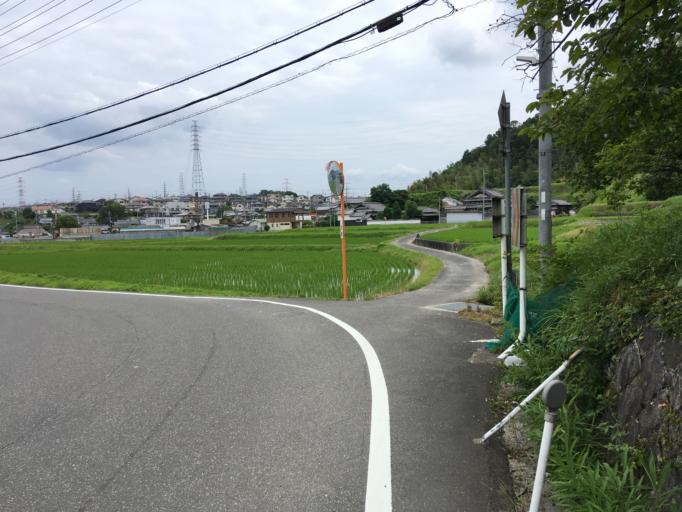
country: JP
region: Nara
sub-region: Ikoma-shi
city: Ikoma
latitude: 34.7209
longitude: 135.7047
